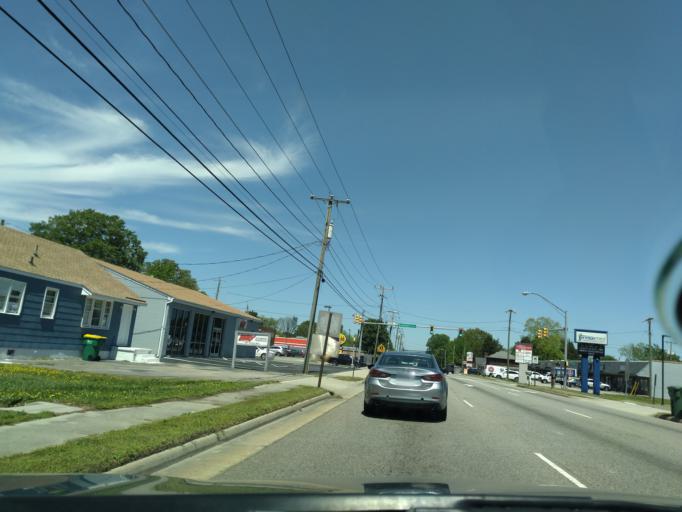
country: US
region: Virginia
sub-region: Prince George County
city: Fort Lee
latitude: 37.2741
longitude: -77.3133
